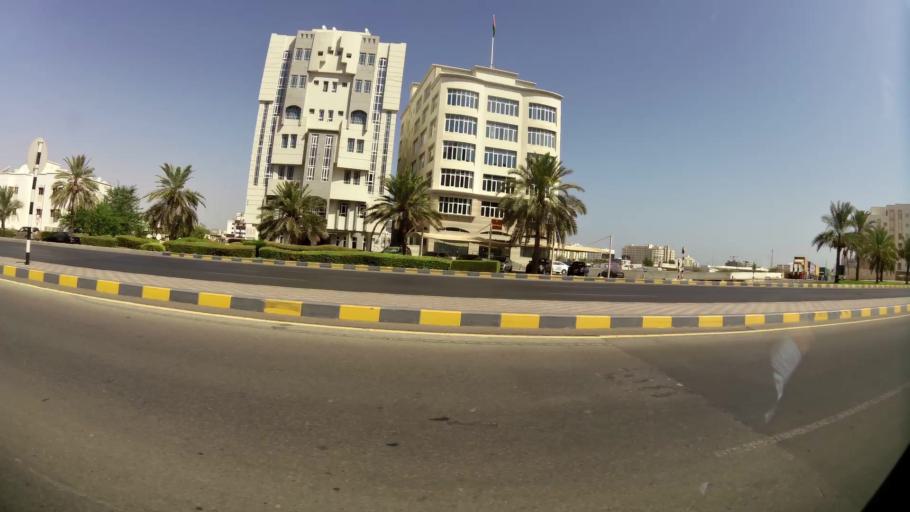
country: OM
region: Muhafazat Masqat
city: Bawshar
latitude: 23.5840
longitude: 58.4088
